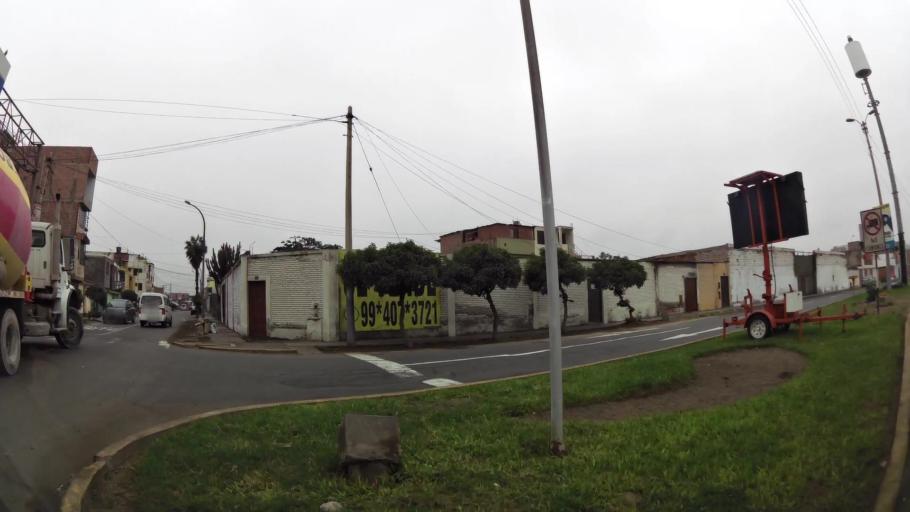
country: PE
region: Callao
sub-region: Callao
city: Callao
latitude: -12.0786
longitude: -77.1111
